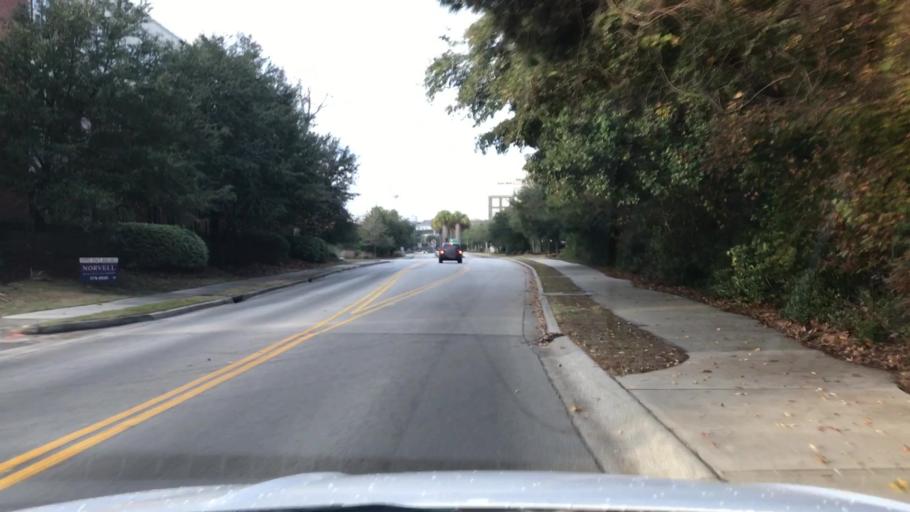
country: US
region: South Carolina
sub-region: Charleston County
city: Mount Pleasant
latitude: 32.8040
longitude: -79.8973
